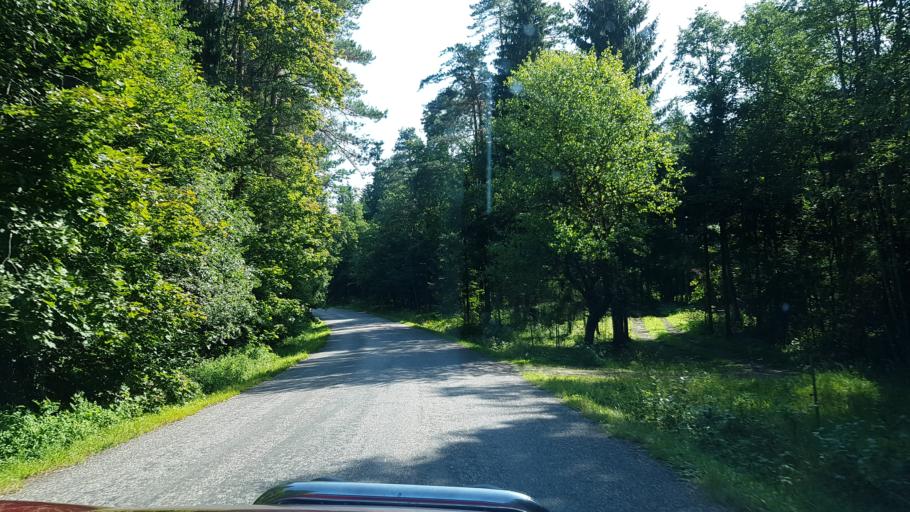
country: EE
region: Vorumaa
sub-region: Voru linn
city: Voru
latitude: 57.7182
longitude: 27.0889
